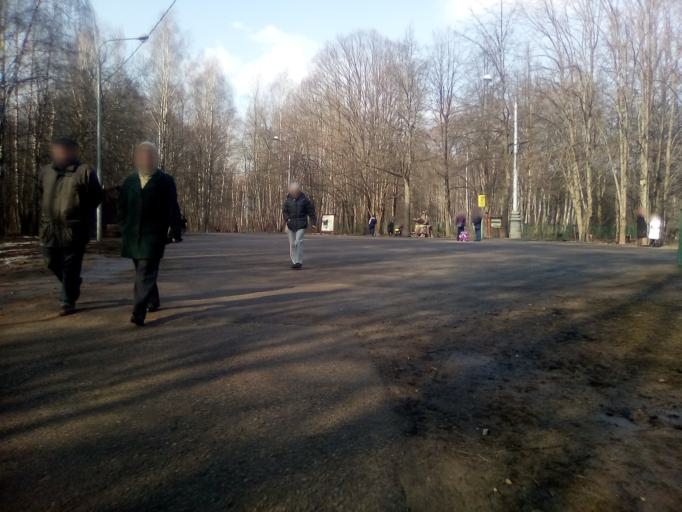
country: RU
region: Moscow
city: Nikulino
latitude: 55.6509
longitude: 37.4635
